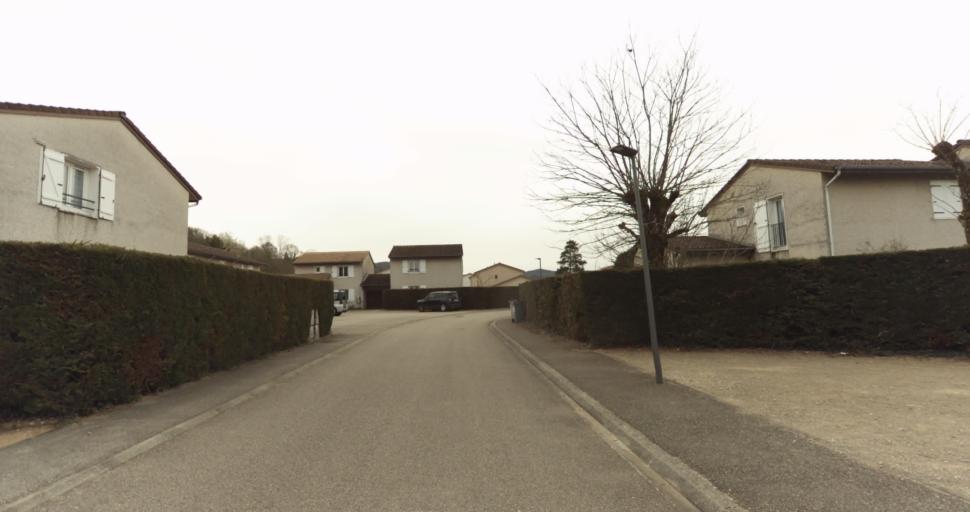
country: FR
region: Rhone-Alpes
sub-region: Departement de l'Ain
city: Amberieu-en-Bugey
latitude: 45.9742
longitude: 5.3532
